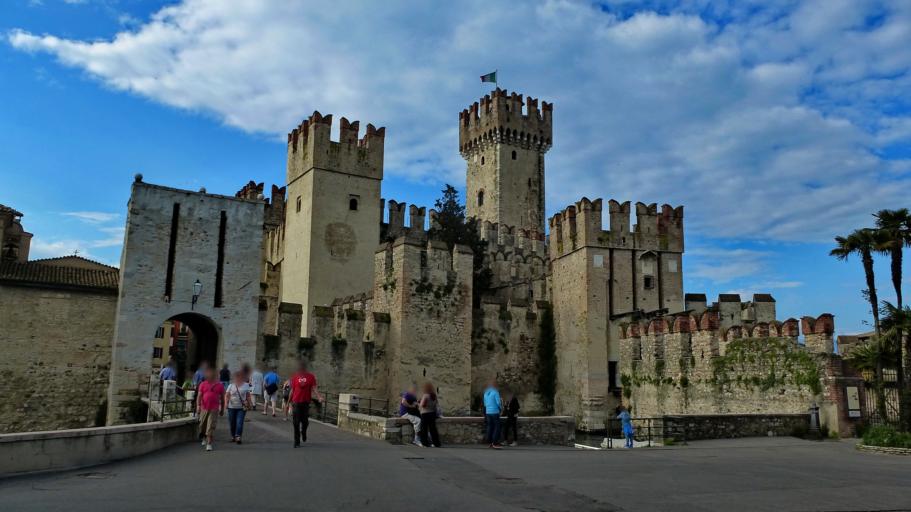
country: IT
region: Lombardy
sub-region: Provincia di Brescia
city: Sirmione
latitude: 45.4917
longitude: 10.6082
